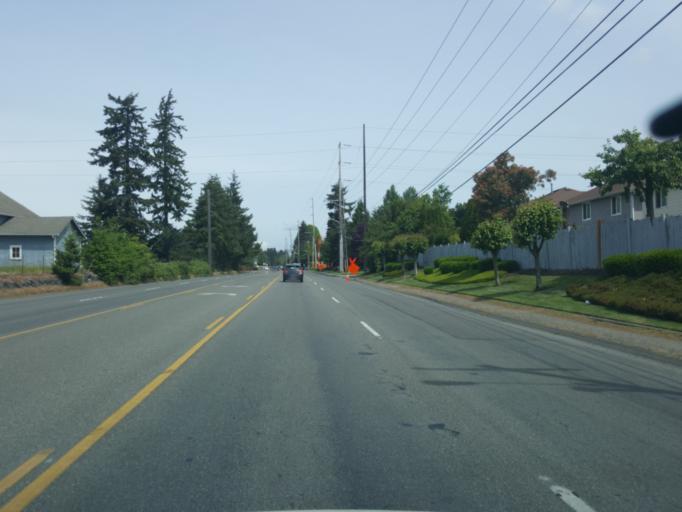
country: US
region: Washington
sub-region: Pierce County
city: Lakewood
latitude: 47.1853
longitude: -122.5086
